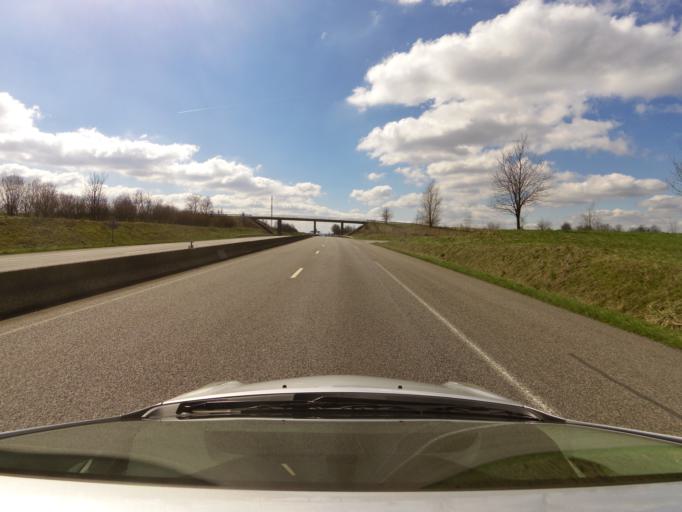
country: FR
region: Haute-Normandie
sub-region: Departement de la Seine-Maritime
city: Neufchatel-en-Bray
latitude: 49.7446
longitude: 1.4744
